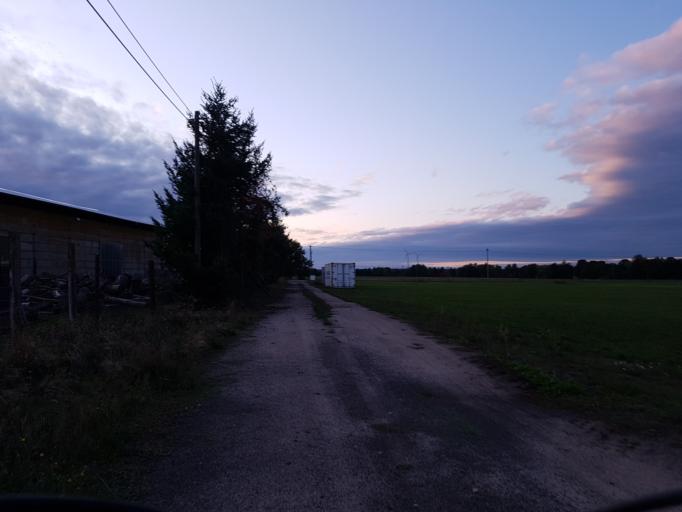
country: DE
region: Brandenburg
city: Schilda
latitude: 51.6109
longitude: 13.3583
